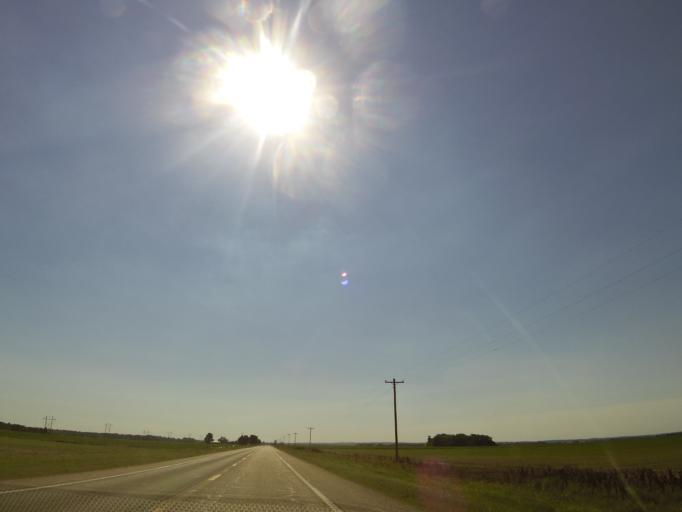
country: US
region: Arkansas
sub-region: Clay County
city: Corning
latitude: 36.4352
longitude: -90.4559
